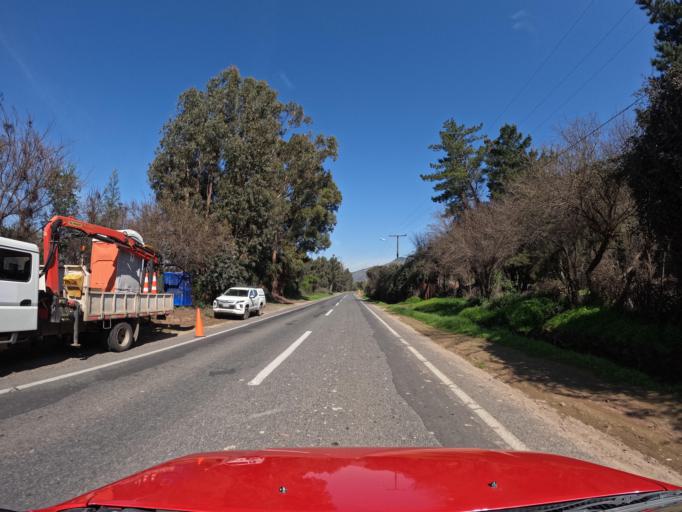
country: CL
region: Maule
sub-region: Provincia de Curico
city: Rauco
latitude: -35.0517
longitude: -71.6027
